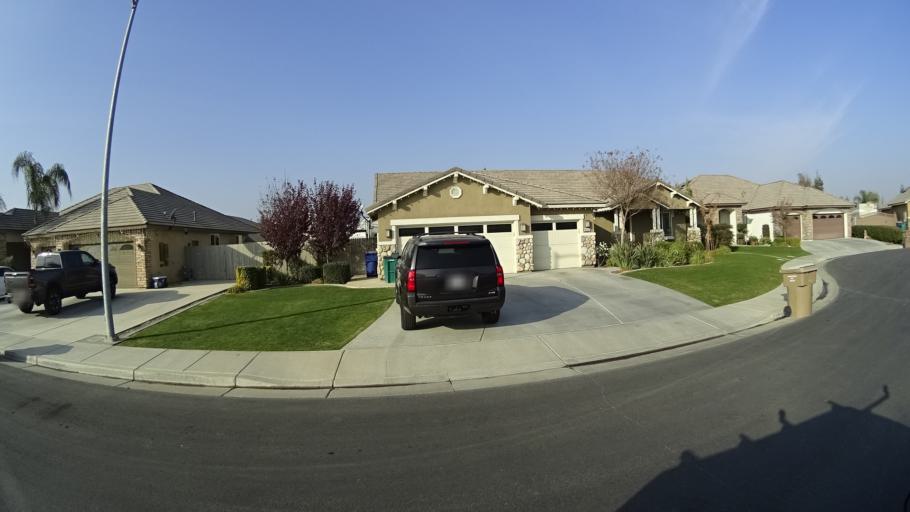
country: US
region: California
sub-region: Kern County
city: Greenacres
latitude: 35.4372
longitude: -119.1197
